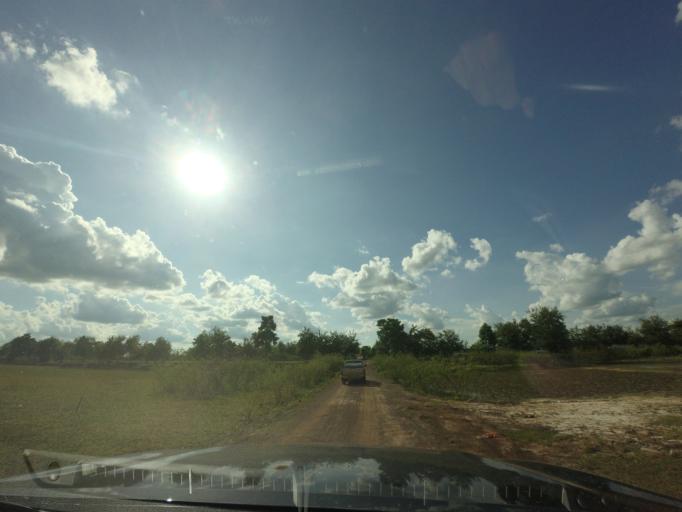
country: TH
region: Changwat Udon Thani
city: Ban Dung
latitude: 17.7453
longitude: 103.3576
